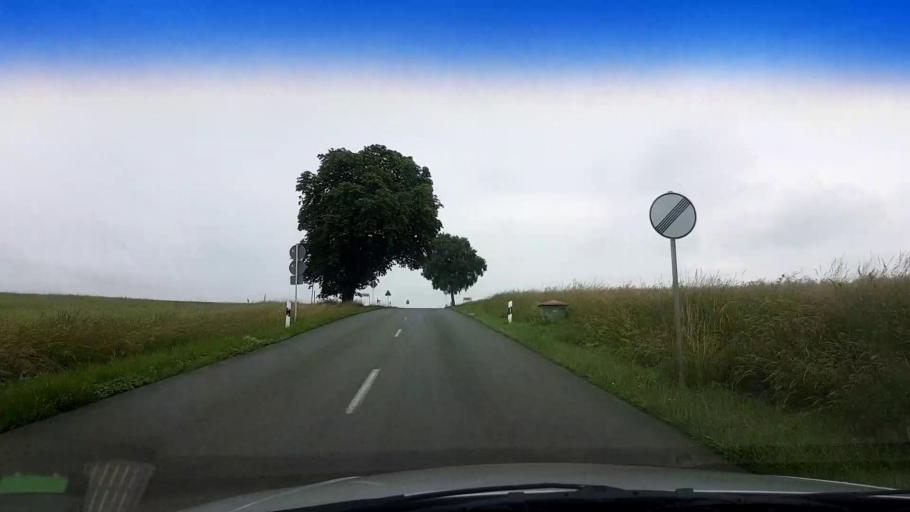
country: DE
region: Bavaria
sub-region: Upper Franconia
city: Kasendorf
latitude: 50.0706
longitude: 11.3357
